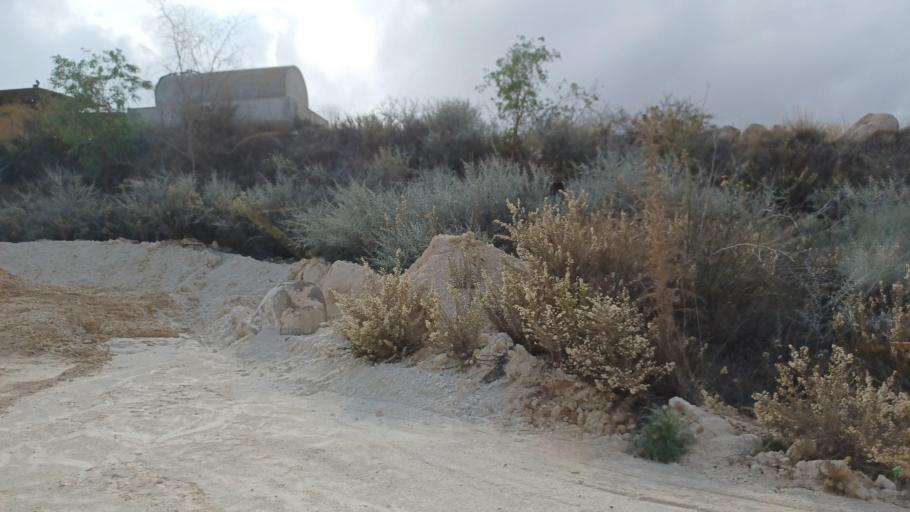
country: CY
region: Pafos
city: Polis
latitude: 35.0001
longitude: 32.3928
